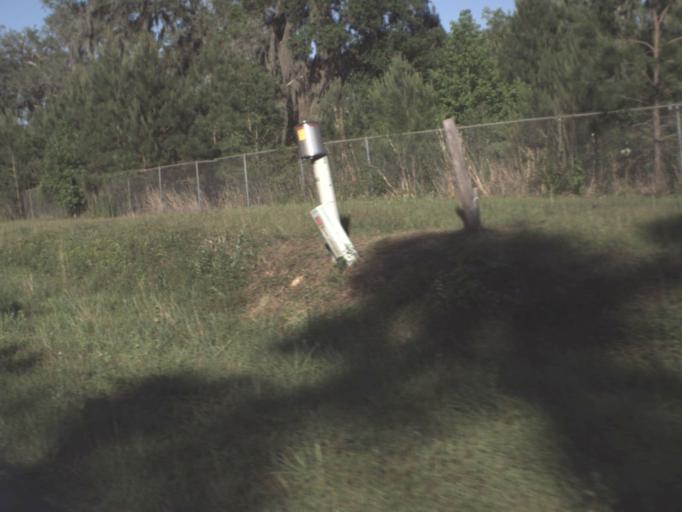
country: US
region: Florida
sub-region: Marion County
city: Dunnellon
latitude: 29.1687
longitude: -82.3385
